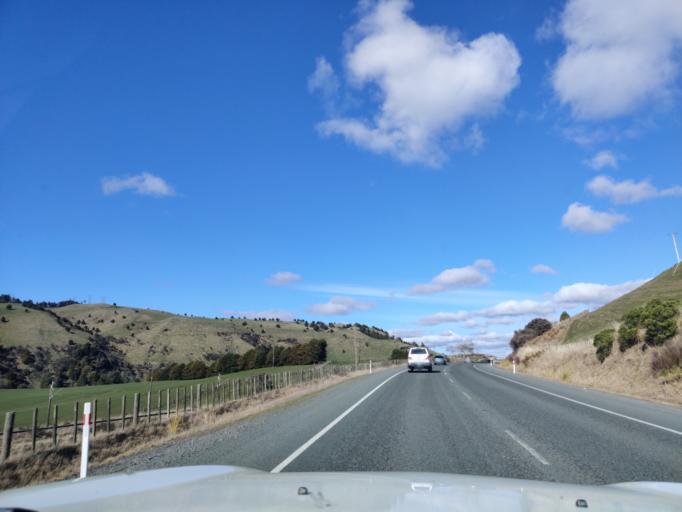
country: NZ
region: Manawatu-Wanganui
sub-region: Ruapehu District
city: Waiouru
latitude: -39.5566
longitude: 175.6981
